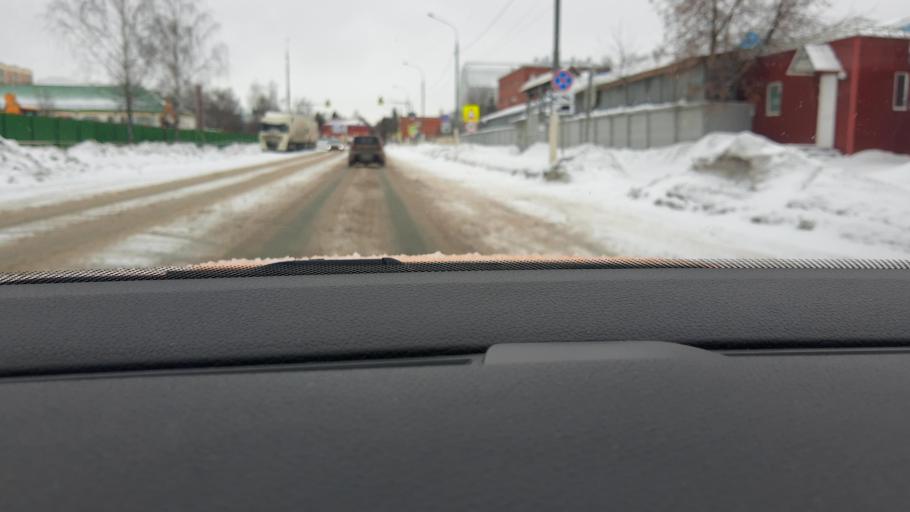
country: RU
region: Moskovskaya
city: Dolgoprudnyy
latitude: 55.9252
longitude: 37.4942
